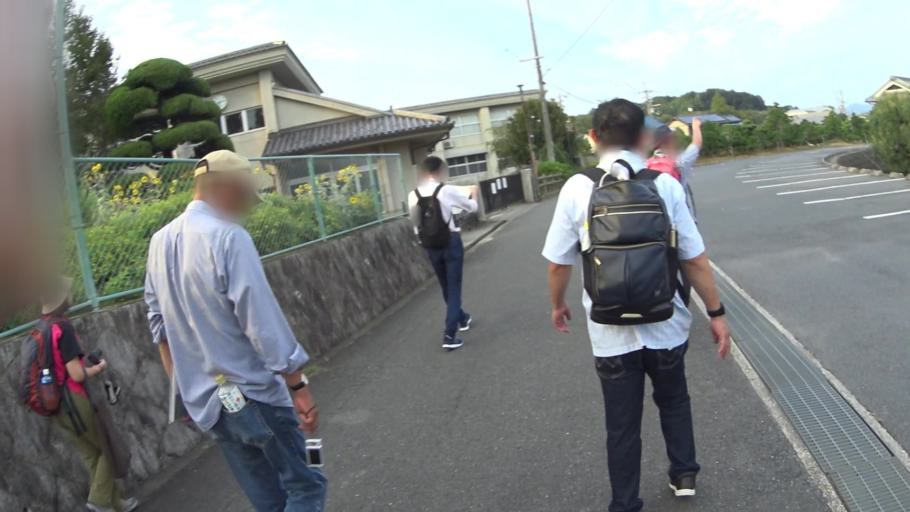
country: JP
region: Nara
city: Kashihara-shi
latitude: 34.4698
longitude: 135.8070
